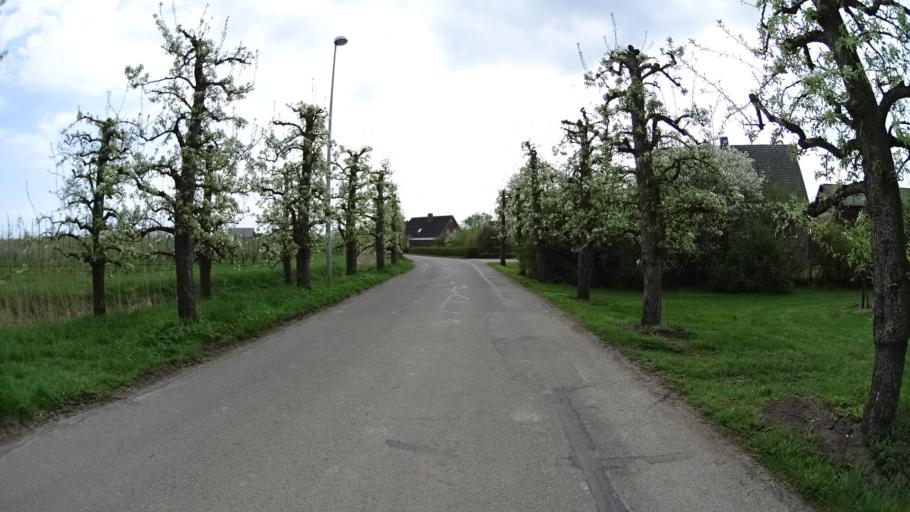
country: DE
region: Lower Saxony
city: Jork
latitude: 53.5347
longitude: 9.7384
